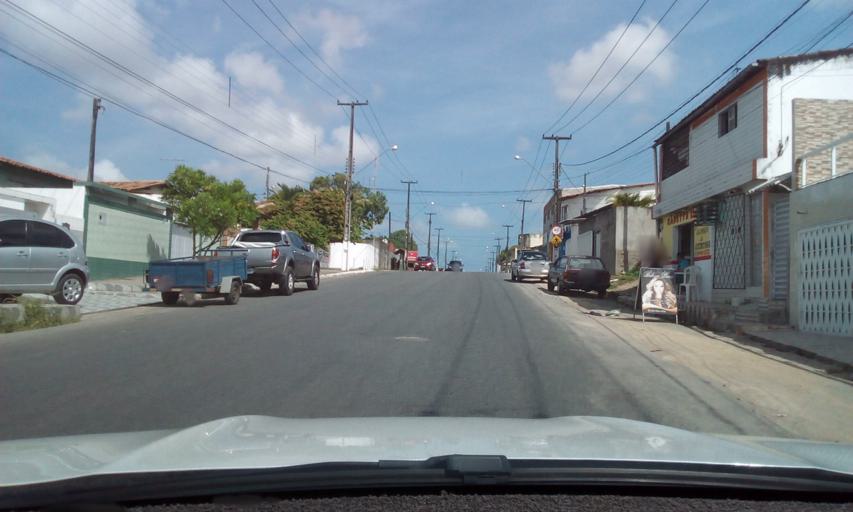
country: BR
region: Paraiba
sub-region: Joao Pessoa
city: Joao Pessoa
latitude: -7.1797
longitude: -34.8835
